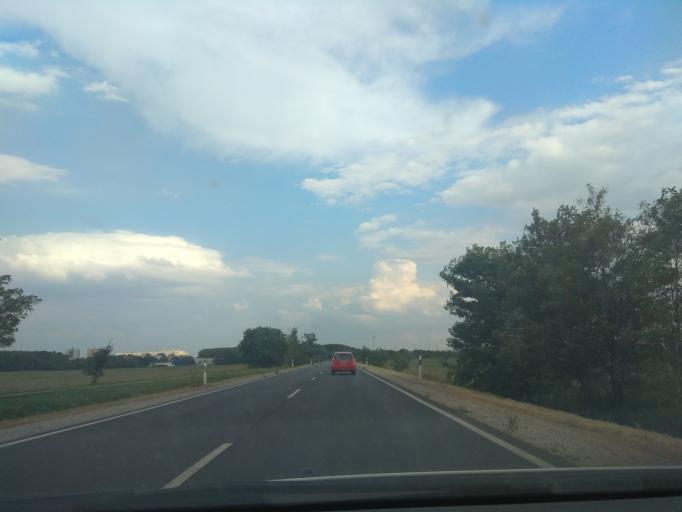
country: HU
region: Borsod-Abauj-Zemplen
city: Sajoszoged
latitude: 47.9339
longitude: 21.0153
